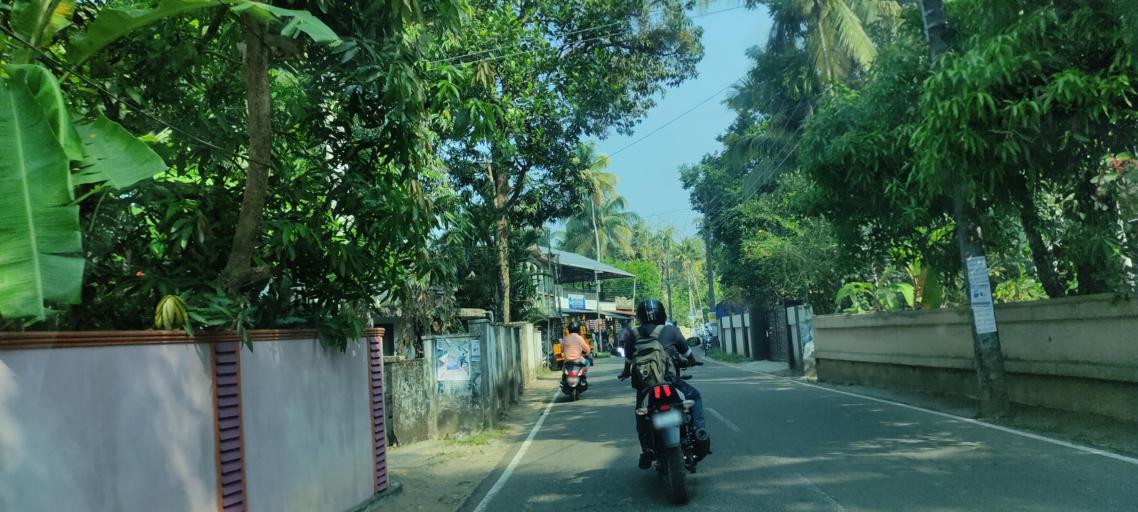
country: IN
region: Kerala
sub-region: Alappuzha
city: Kutiatodu
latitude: 9.7713
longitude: 76.3081
